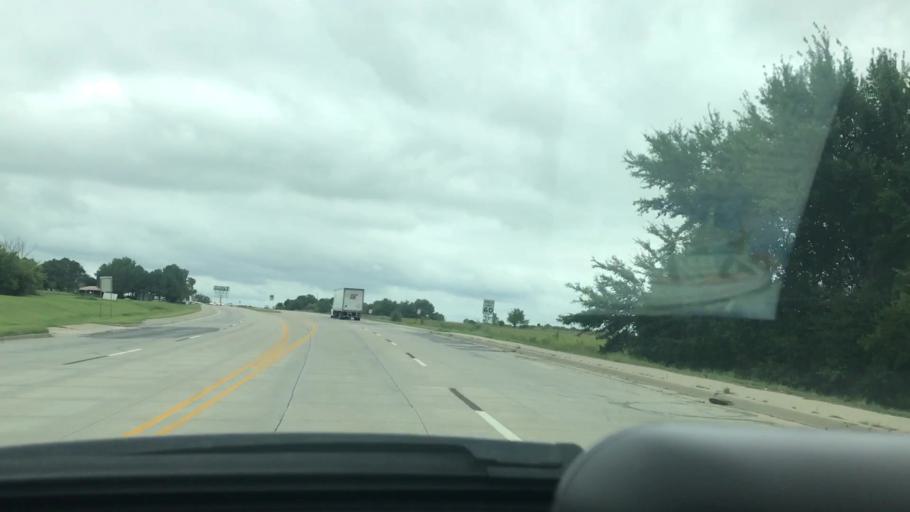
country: US
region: Oklahoma
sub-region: Pittsburg County
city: McAlester
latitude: 34.7280
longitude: -95.8980
